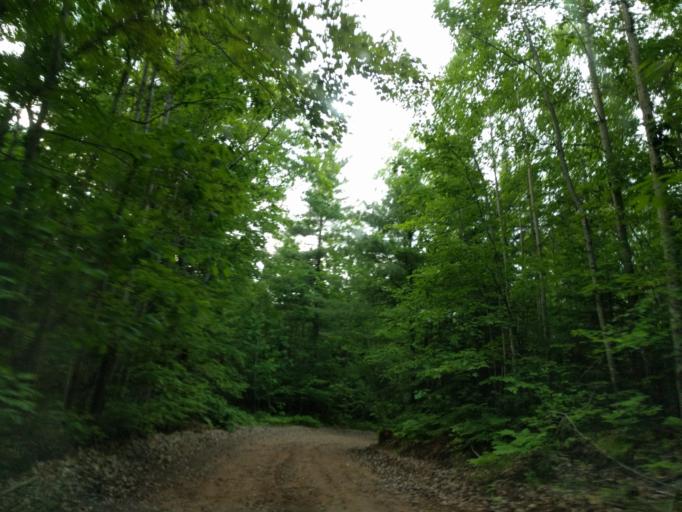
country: US
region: Michigan
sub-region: Marquette County
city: Trowbridge Park
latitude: 46.6086
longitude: -87.5081
